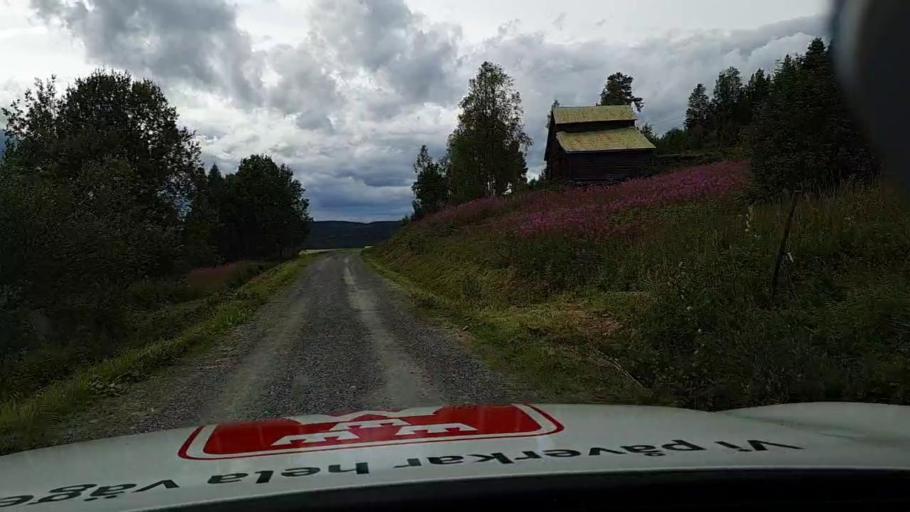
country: SE
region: Jaemtland
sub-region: Krokoms Kommun
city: Valla
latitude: 63.5841
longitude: 13.9928
